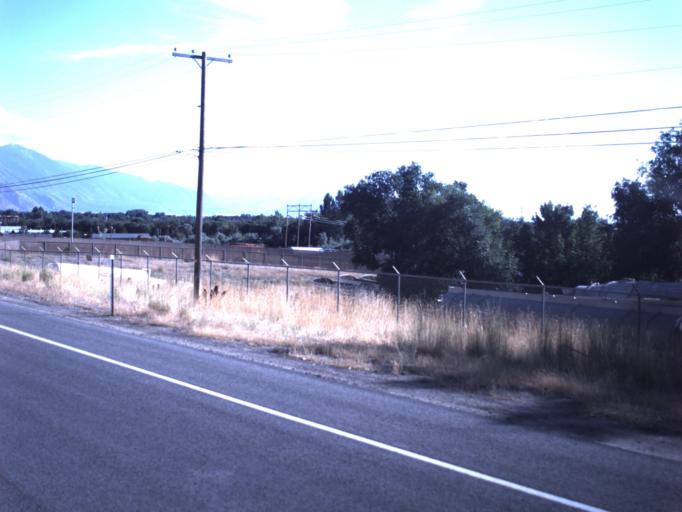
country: US
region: Utah
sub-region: Utah County
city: Springville
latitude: 40.1902
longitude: -111.6117
